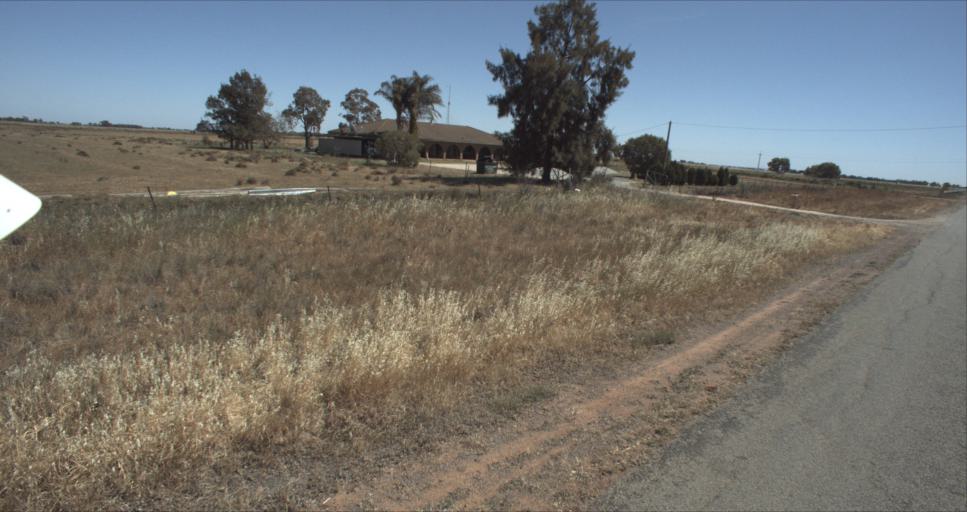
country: AU
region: New South Wales
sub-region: Leeton
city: Leeton
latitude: -34.5693
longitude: 146.3109
